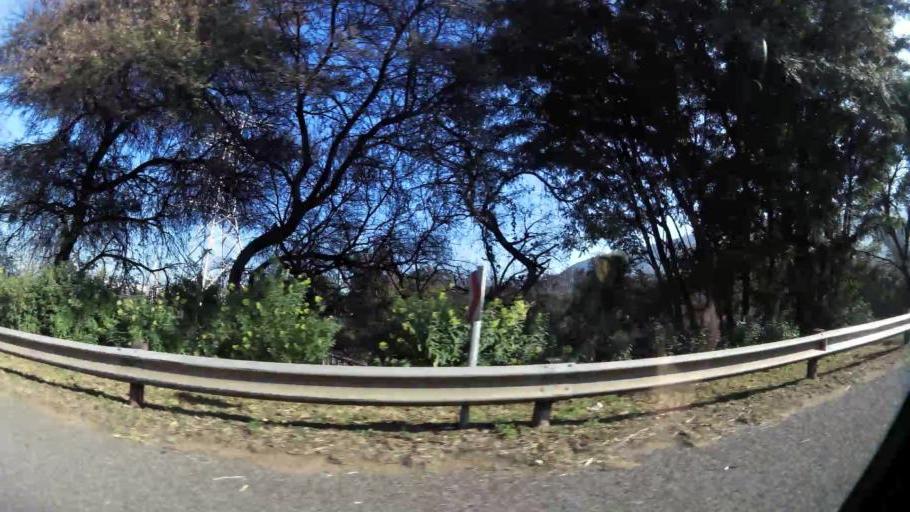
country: ZA
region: Gauteng
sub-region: City of Tshwane Metropolitan Municipality
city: Pretoria
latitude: -25.7020
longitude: 28.1723
